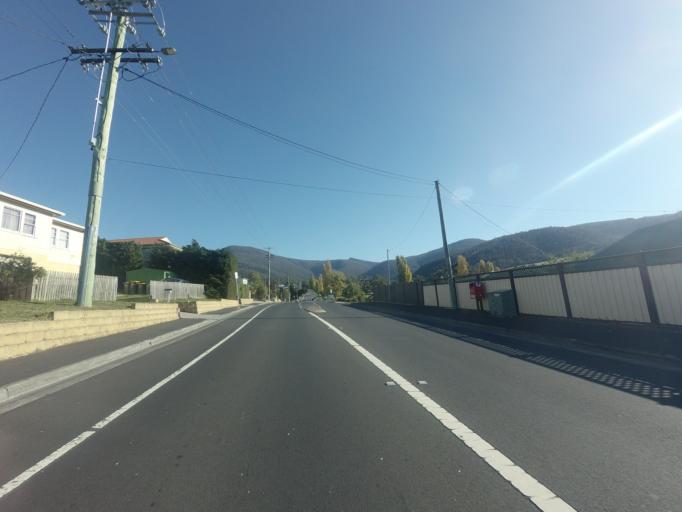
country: AU
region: Tasmania
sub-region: Glenorchy
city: West Moonah
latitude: -42.8480
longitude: 147.2613
